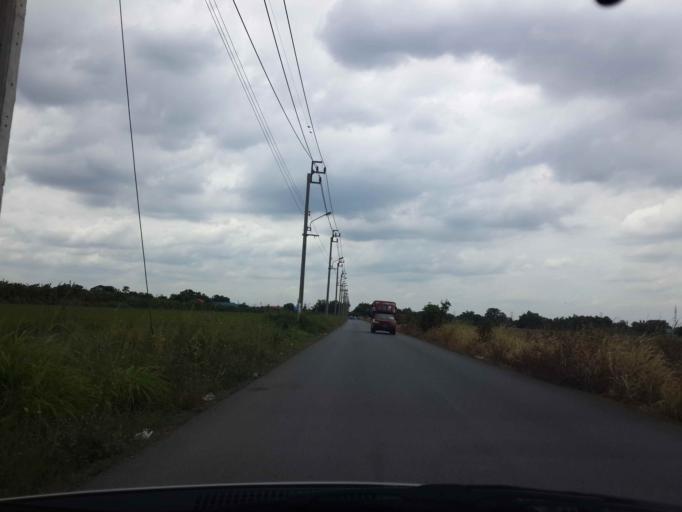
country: TH
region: Bangkok
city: Khlong Sam Wa
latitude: 13.8867
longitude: 100.7039
